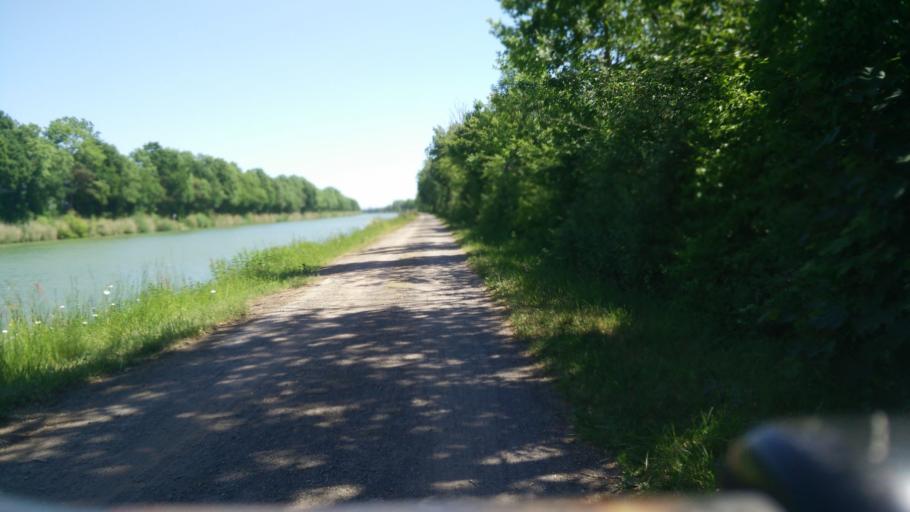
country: DE
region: Lower Saxony
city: Wunstorf
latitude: 52.3933
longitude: 9.4281
